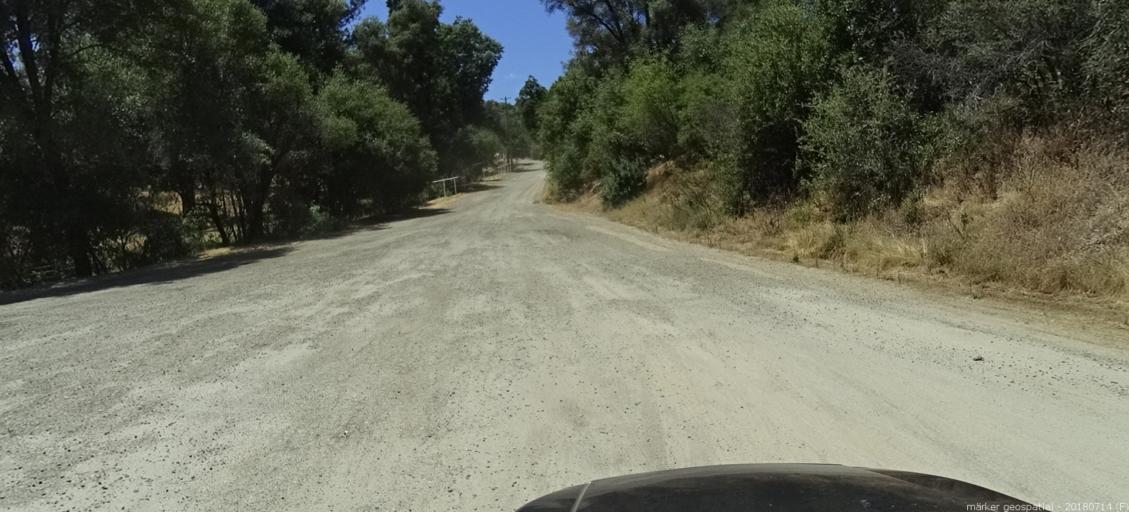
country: US
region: California
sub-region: Madera County
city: Ahwahnee
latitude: 37.4092
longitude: -119.7180
